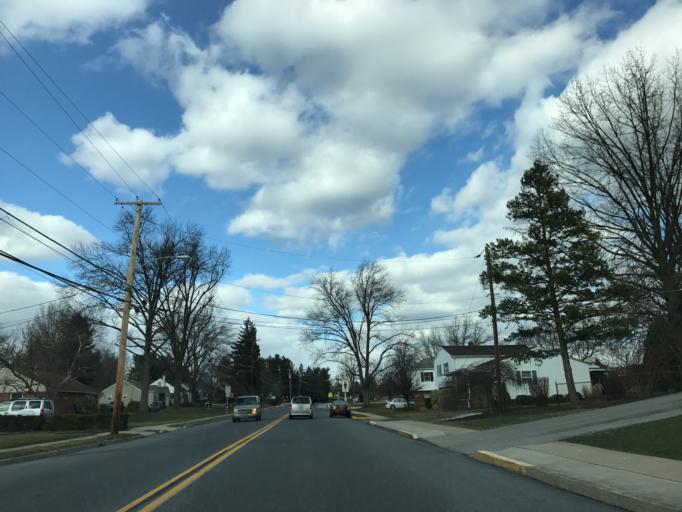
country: US
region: Pennsylvania
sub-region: Lancaster County
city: Elizabethtown
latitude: 40.1553
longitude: -76.5967
